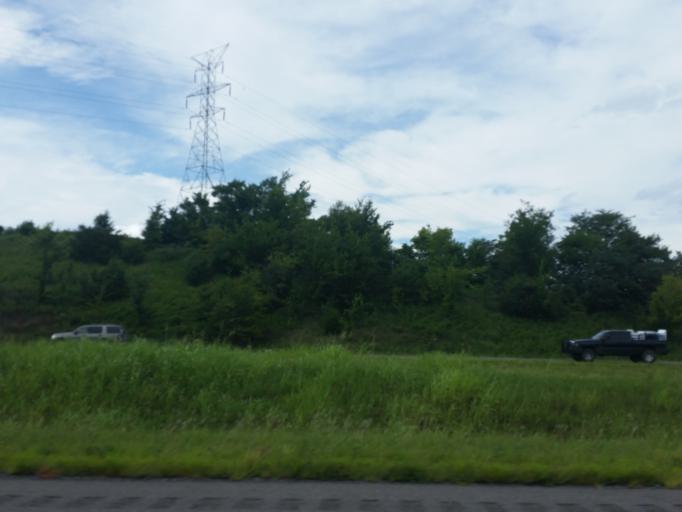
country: US
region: Kentucky
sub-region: Marshall County
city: Calvert City
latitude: 37.0457
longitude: -88.2569
